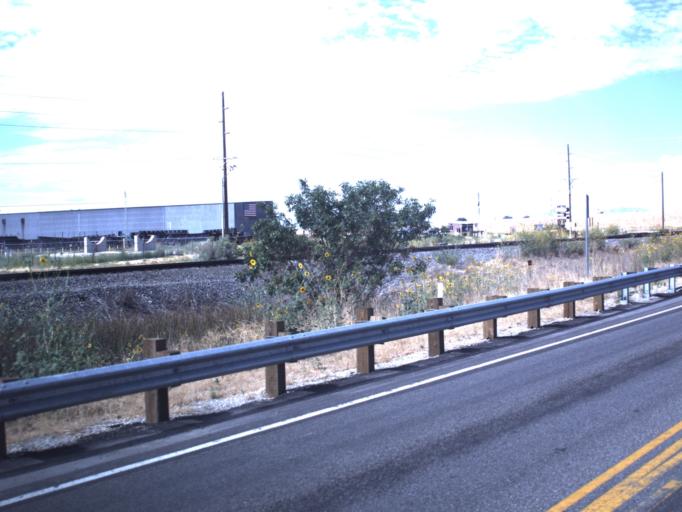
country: US
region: Utah
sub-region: Box Elder County
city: Brigham City
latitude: 41.5343
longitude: -112.0599
